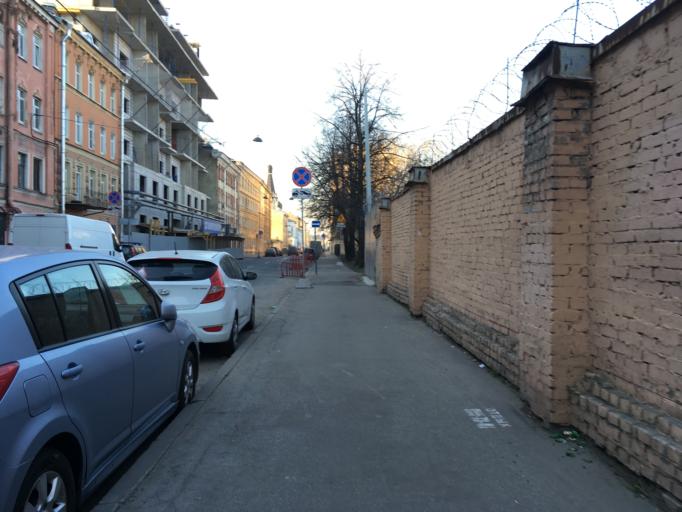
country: RU
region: St.-Petersburg
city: Centralniy
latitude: 59.9158
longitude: 30.3611
